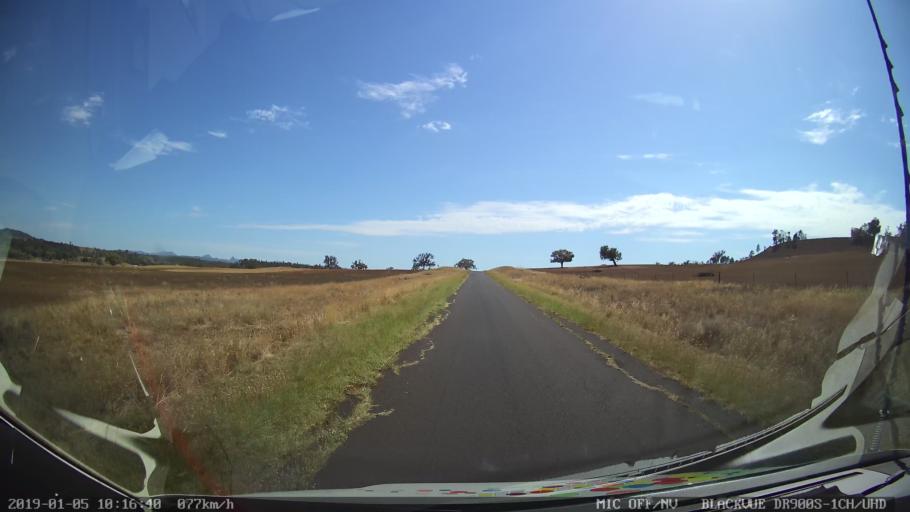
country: AU
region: New South Wales
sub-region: Gilgandra
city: Gilgandra
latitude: -31.5731
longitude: 148.9545
